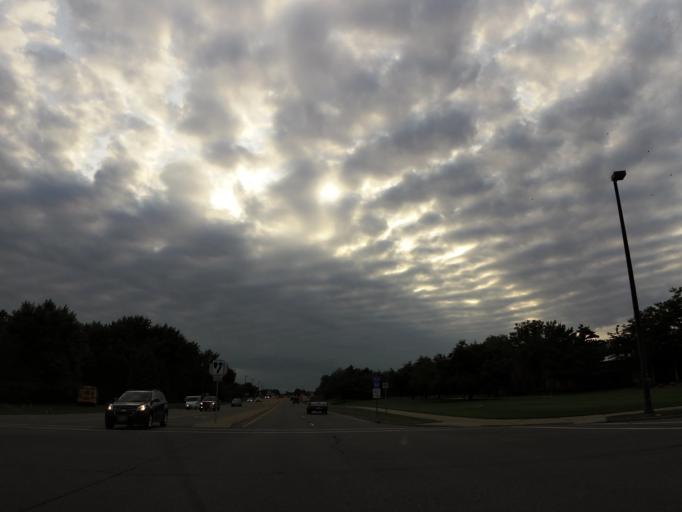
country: US
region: Minnesota
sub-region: Dakota County
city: Lakeville
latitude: 44.6561
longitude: -93.2427
